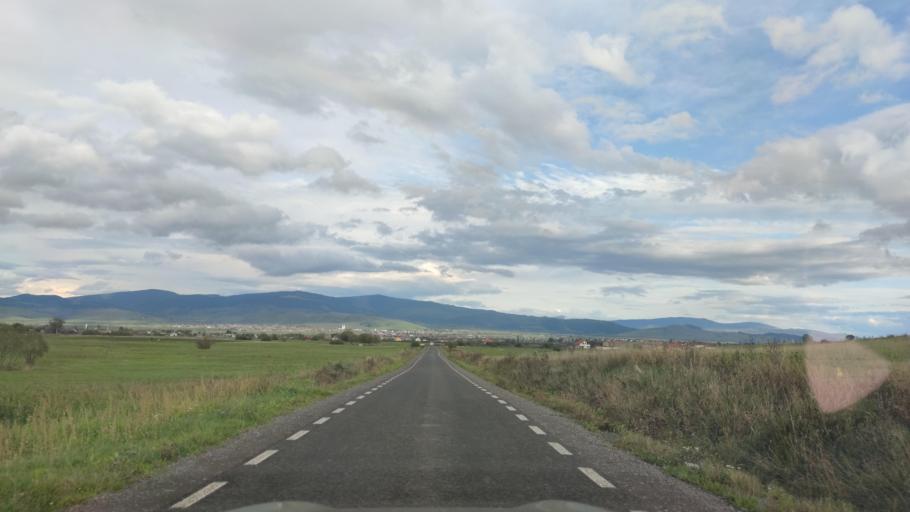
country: RO
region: Harghita
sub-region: Comuna Remetea
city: Remetea
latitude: 46.8057
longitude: 25.4273
